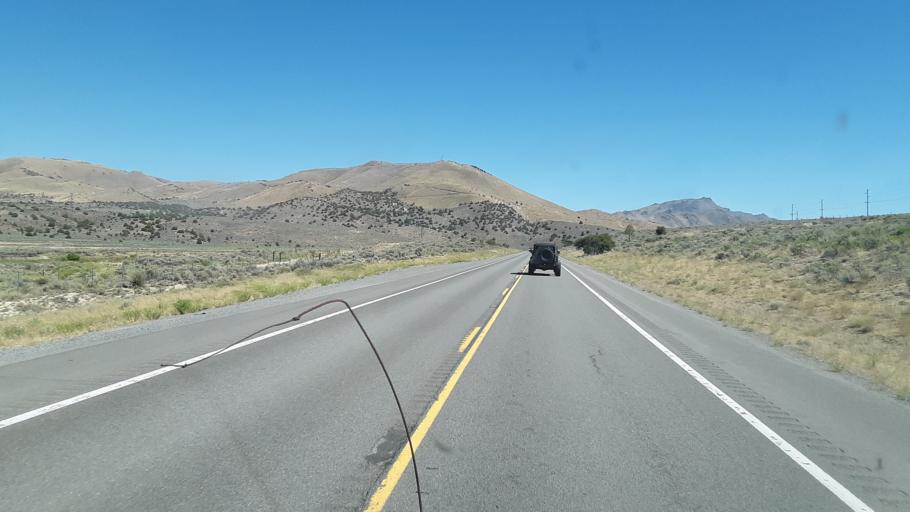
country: US
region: Nevada
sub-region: Washoe County
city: Cold Springs
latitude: 39.9451
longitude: -120.0253
